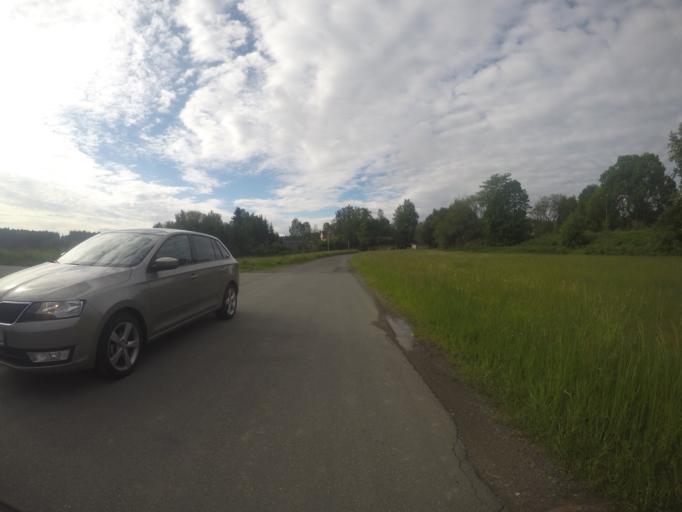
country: DE
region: Bavaria
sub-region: Upper Franconia
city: Schonwald
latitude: 50.1995
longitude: 12.0973
